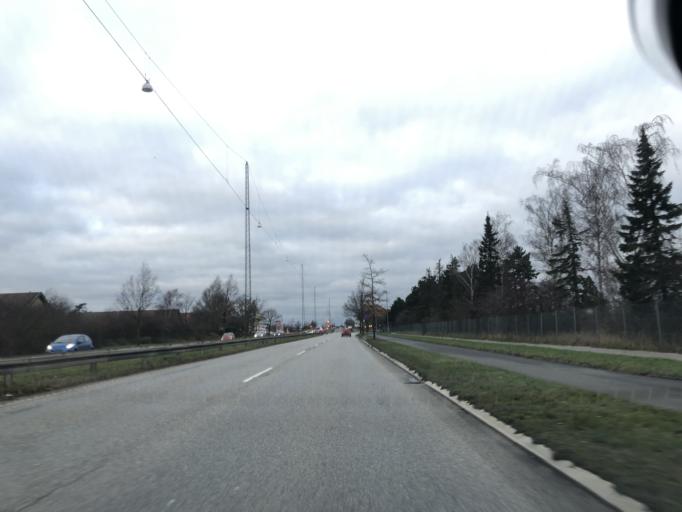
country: DK
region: Capital Region
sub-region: Hvidovre Kommune
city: Hvidovre
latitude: 55.6431
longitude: 12.4626
